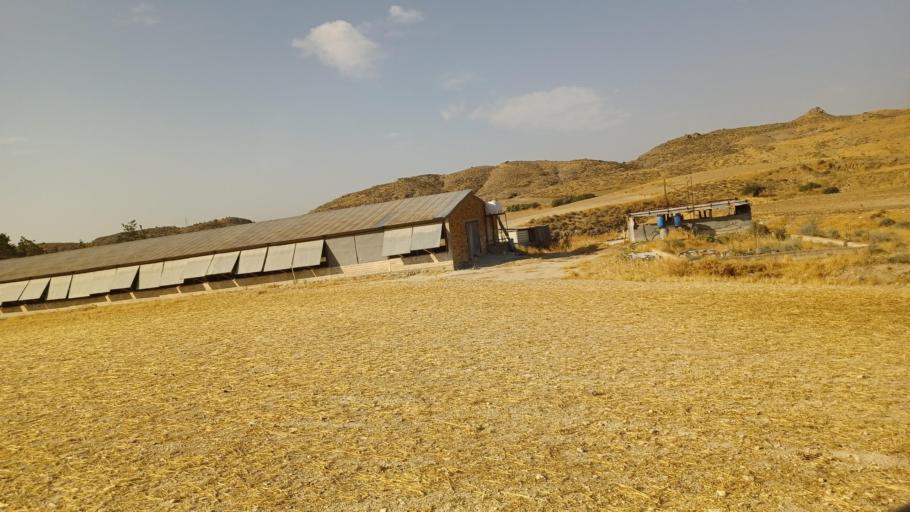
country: CY
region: Larnaka
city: Athienou
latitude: 35.0146
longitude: 33.5608
